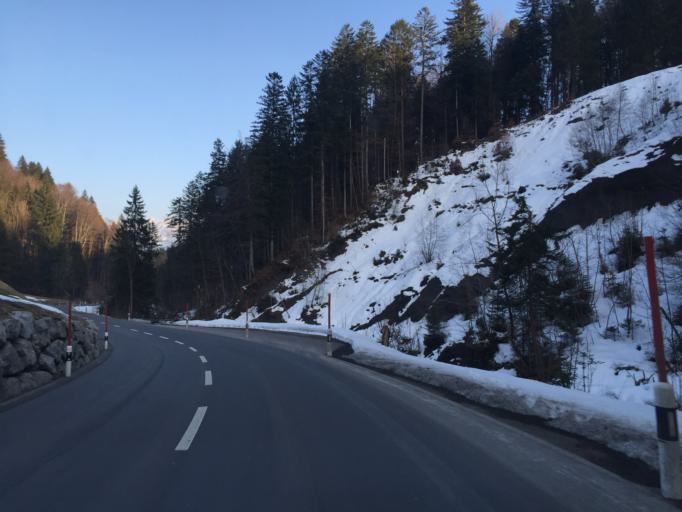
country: CH
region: Saint Gallen
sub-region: Wahlkreis Toggenburg
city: Wildhaus
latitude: 47.1966
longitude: 9.3890
